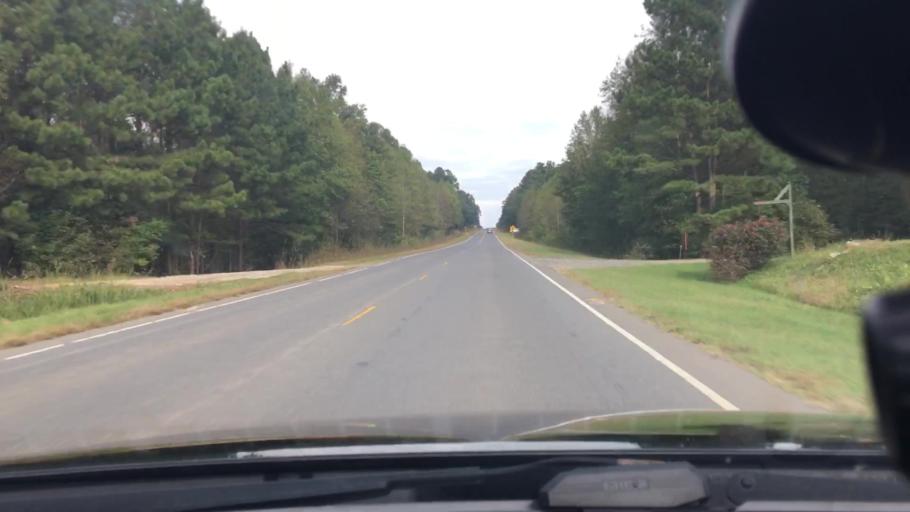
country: US
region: North Carolina
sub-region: Montgomery County
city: Troy
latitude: 35.3159
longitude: -79.9792
